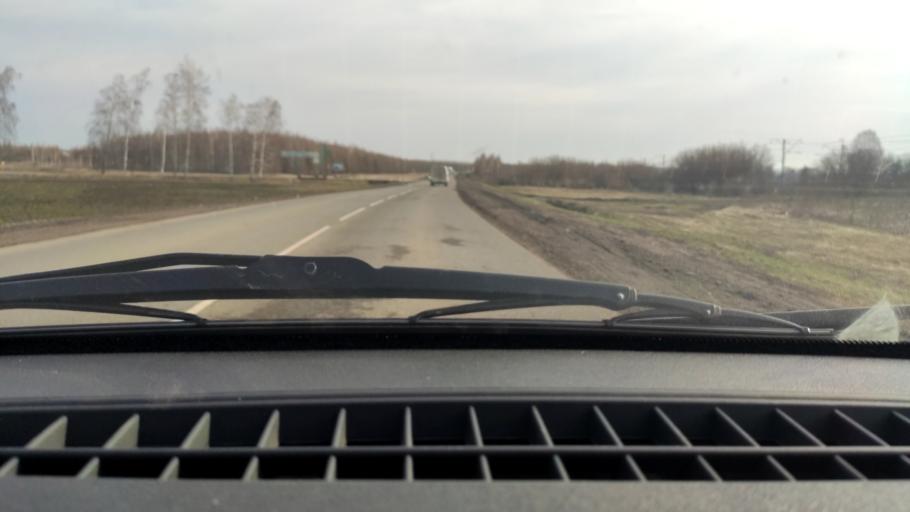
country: RU
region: Bashkortostan
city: Chishmy
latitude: 54.5740
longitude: 55.3573
